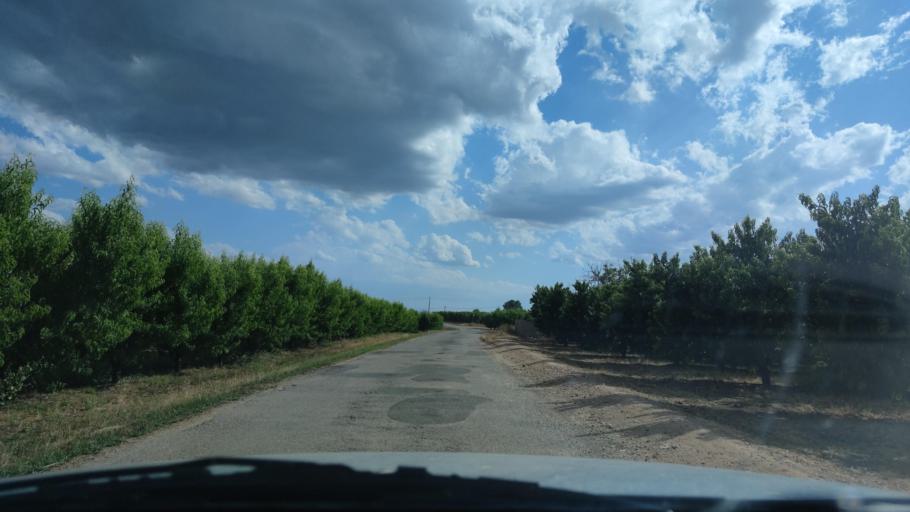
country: ES
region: Catalonia
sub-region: Provincia de Lleida
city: Alcarras
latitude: 41.5821
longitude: 0.5335
